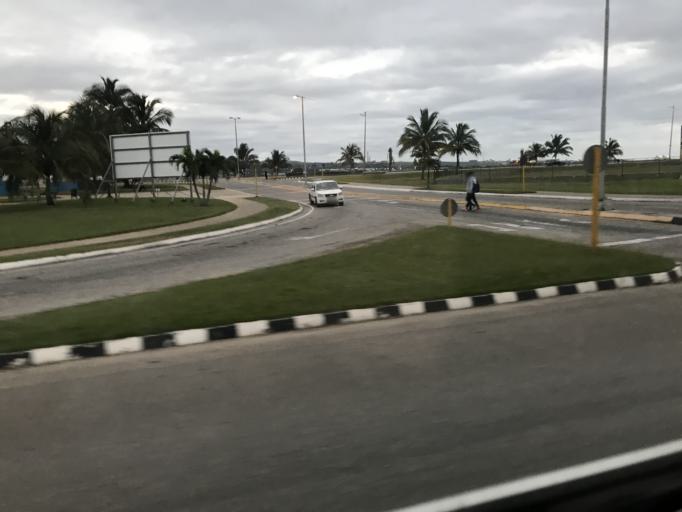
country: CU
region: Matanzas
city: Matanzas
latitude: 23.0364
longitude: -81.5648
